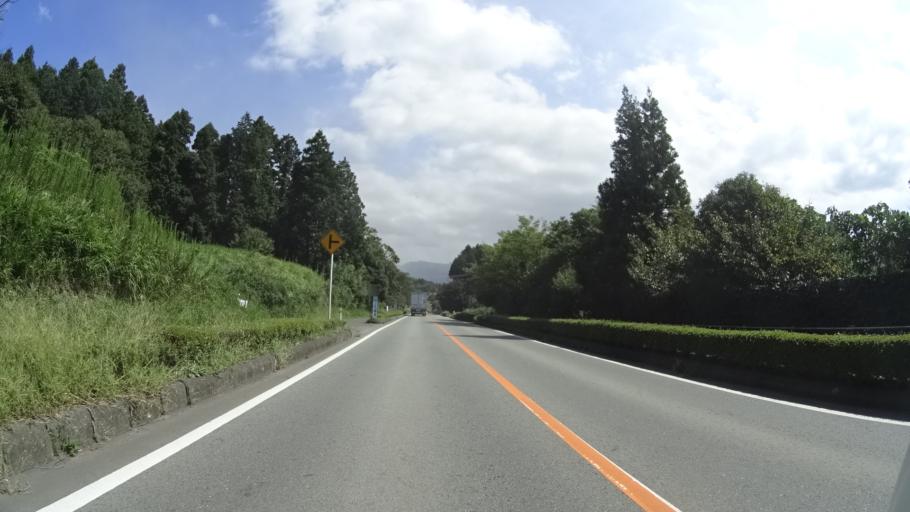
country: JP
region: Kumamoto
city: Aso
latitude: 32.8539
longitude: 131.0194
